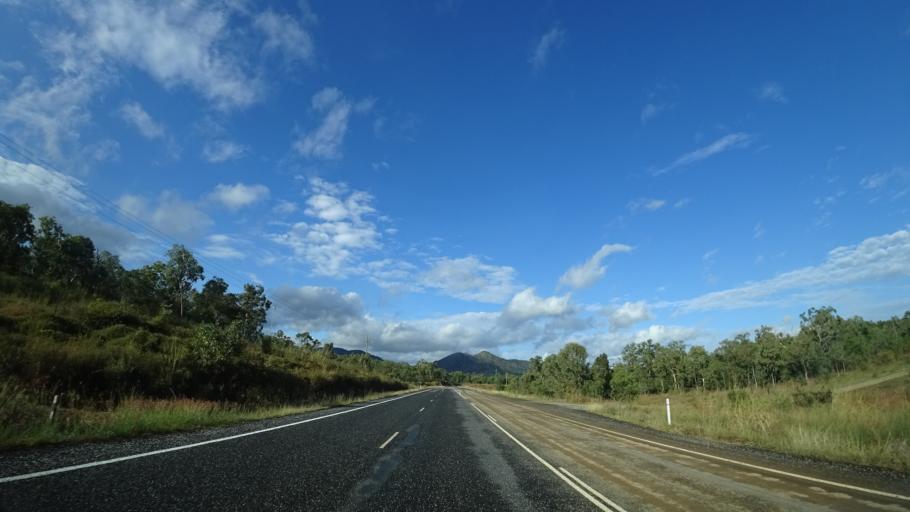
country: AU
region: Queensland
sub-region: Cook
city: Cooktown
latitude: -15.6126
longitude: 145.2213
